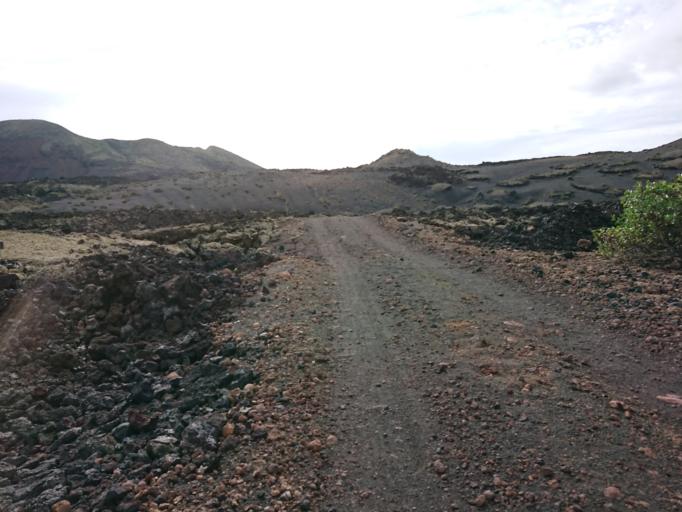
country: ES
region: Canary Islands
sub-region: Provincia de Las Palmas
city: Tinajo
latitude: 29.0142
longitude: -13.6777
